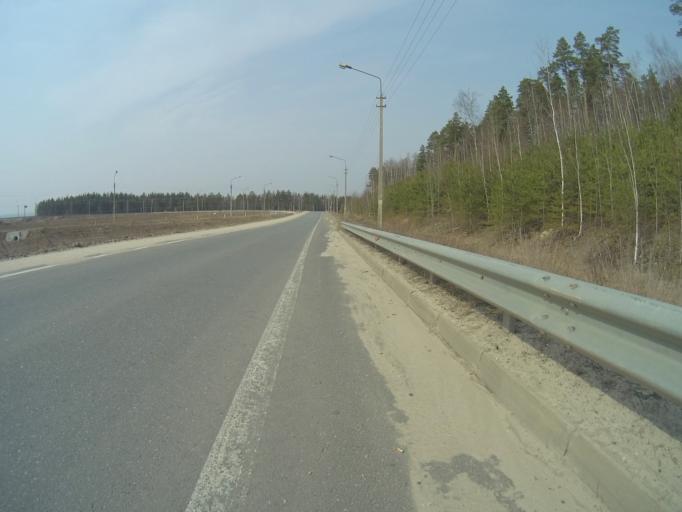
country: RU
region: Vladimir
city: Kommunar
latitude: 56.0582
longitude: 40.4429
